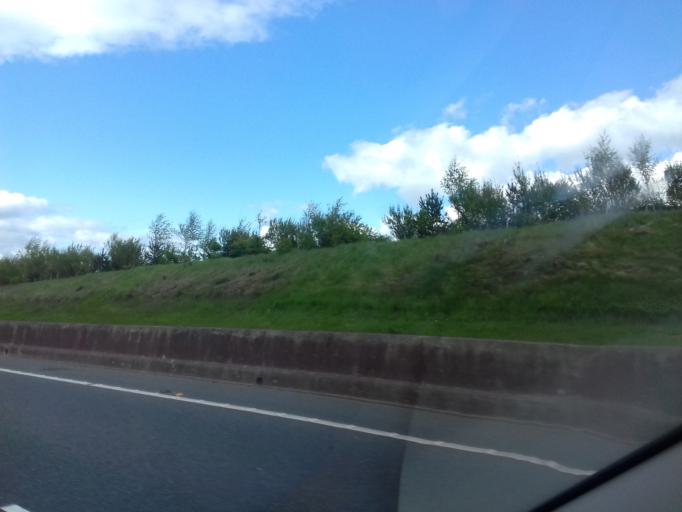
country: IE
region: Leinster
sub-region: Kilkenny
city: Thomastown
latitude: 52.5196
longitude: -7.2383
